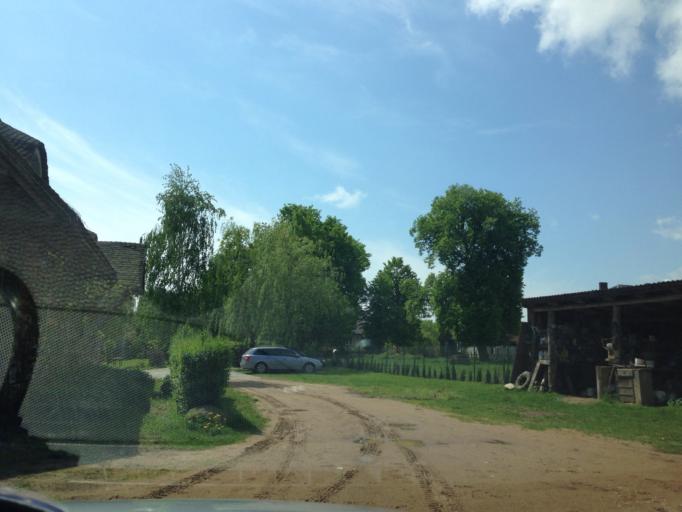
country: PL
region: Podlasie
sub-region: Powiat lomzynski
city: Wizna
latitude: 53.2842
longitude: 22.4577
